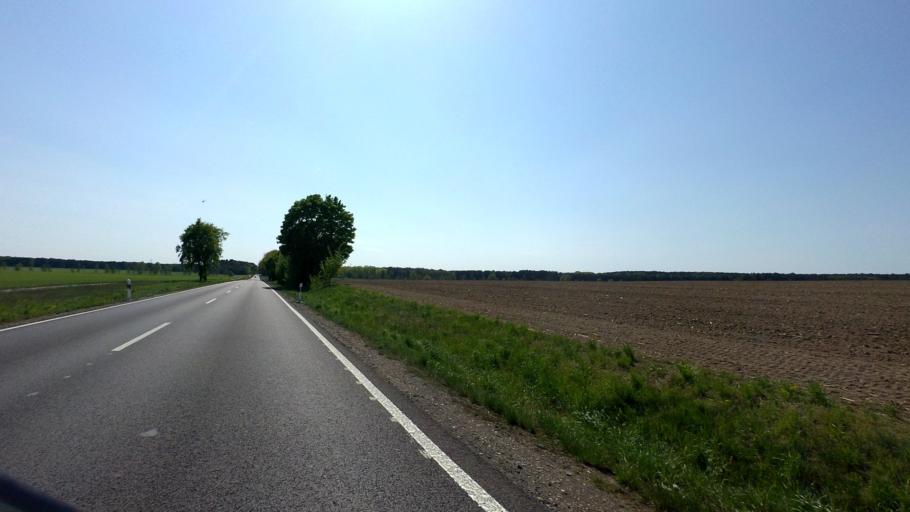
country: DE
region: Brandenburg
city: Tauche
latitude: 52.0755
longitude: 14.1573
